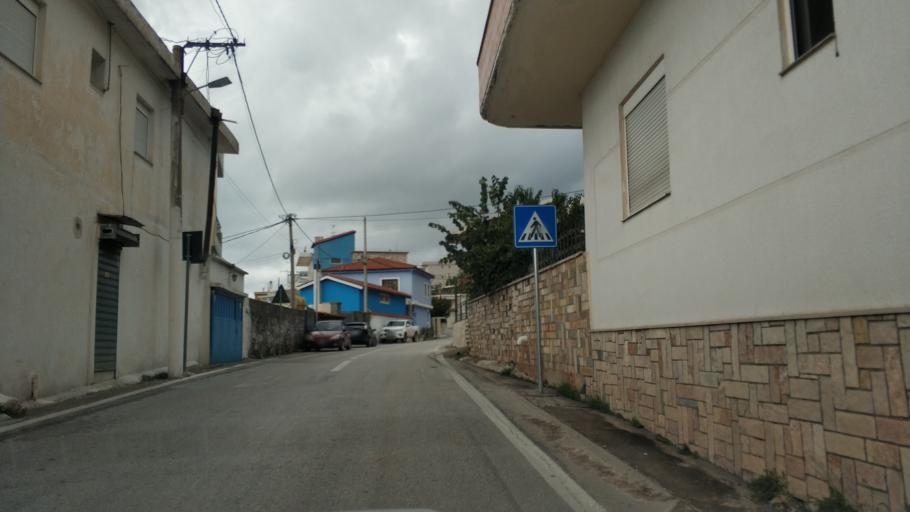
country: AL
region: Vlore
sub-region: Rrethi i Vlores
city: Vranisht
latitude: 40.1562
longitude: 19.6320
